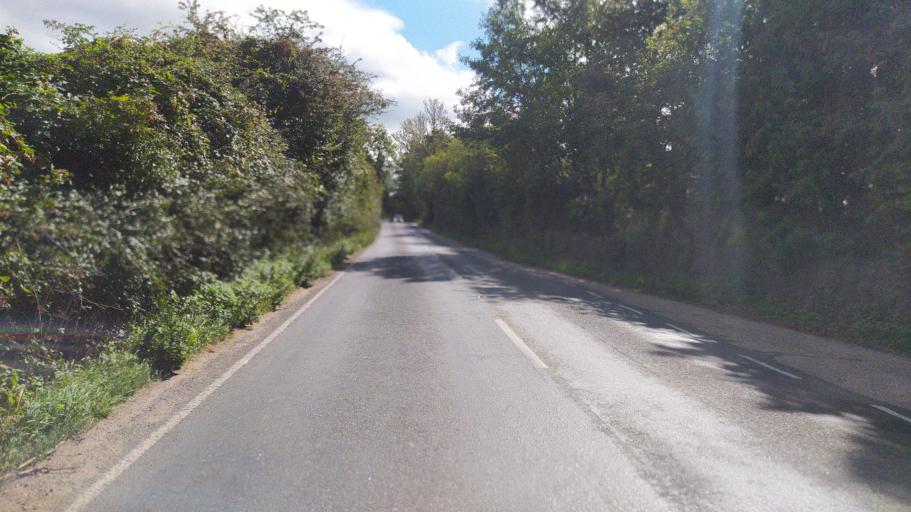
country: GB
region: England
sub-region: Hampshire
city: Romsey
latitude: 51.0121
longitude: -1.5008
